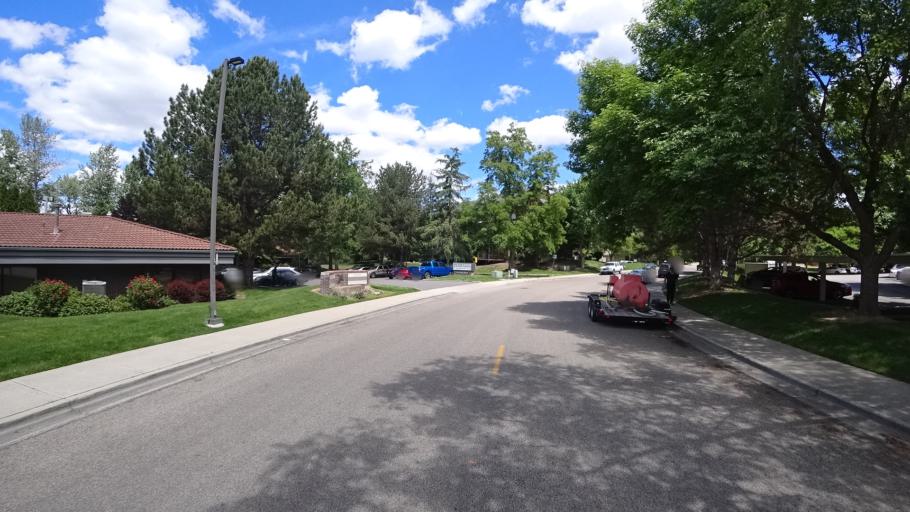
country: US
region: Idaho
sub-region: Ada County
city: Boise
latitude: 43.5957
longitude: -116.1839
